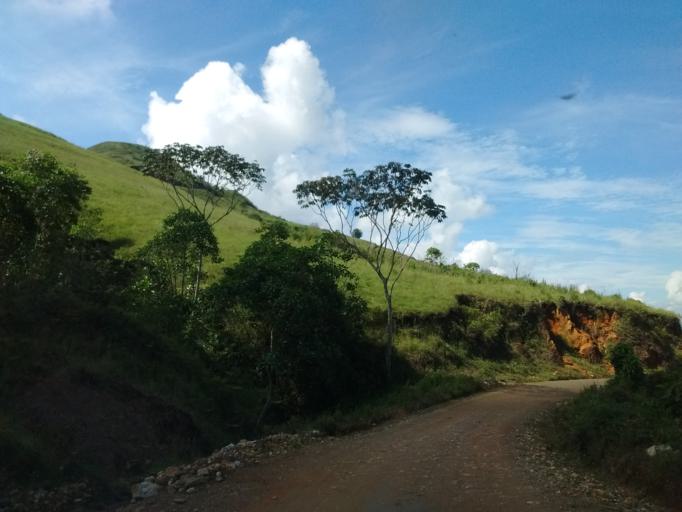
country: CO
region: Cauca
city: Morales
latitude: 2.6916
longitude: -76.7451
